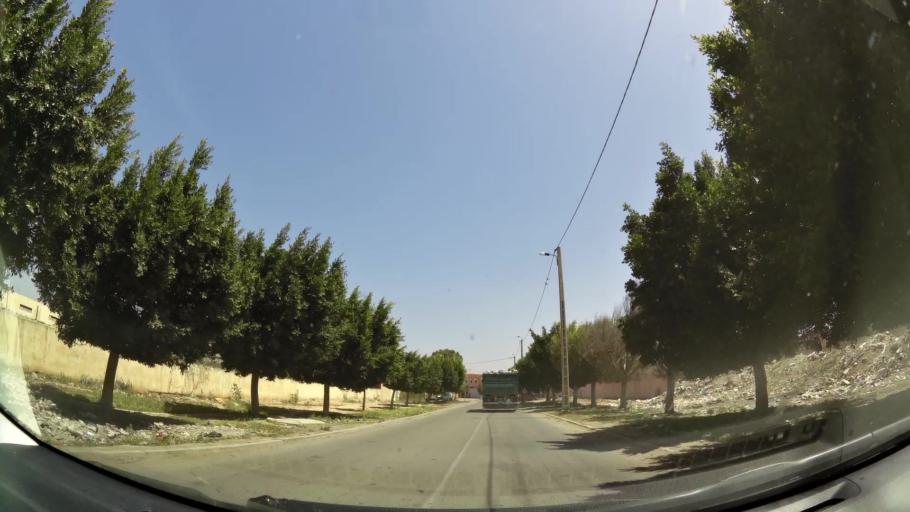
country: MA
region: Souss-Massa-Draa
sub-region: Inezgane-Ait Mellou
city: Inezgane
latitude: 30.3385
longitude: -9.4853
